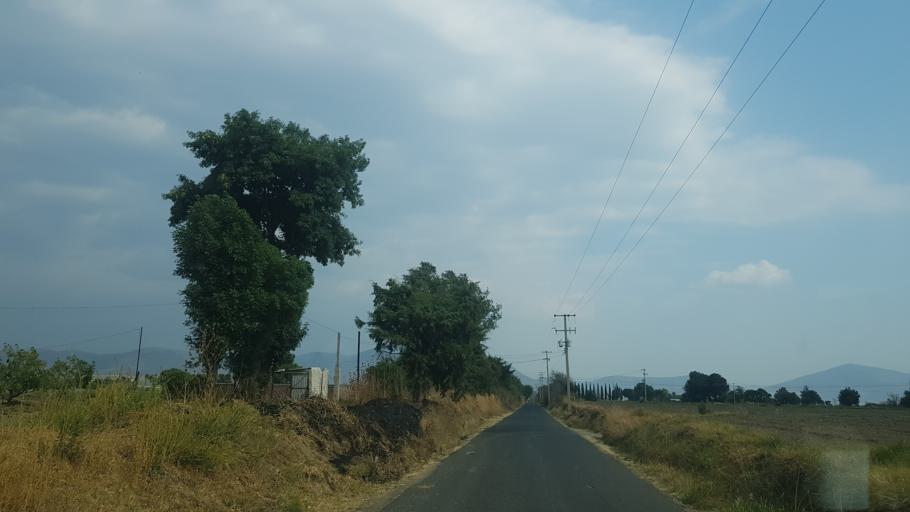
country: MX
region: Puebla
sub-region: Santa Isabel Cholula
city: Santa Ana Acozautla
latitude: 18.9560
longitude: -98.4015
